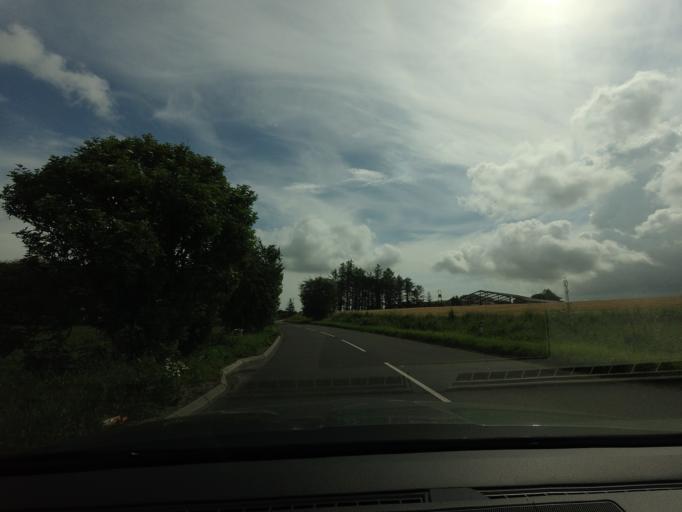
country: GB
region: Scotland
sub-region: Aberdeenshire
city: Mintlaw
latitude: 57.5234
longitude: -1.9676
